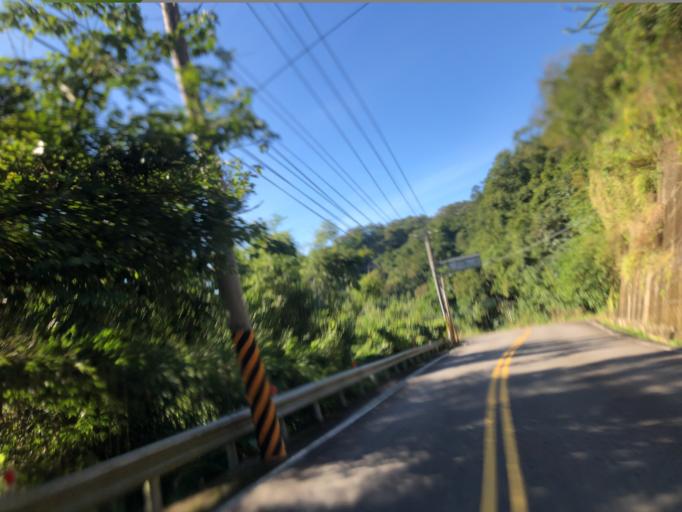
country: TW
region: Taiwan
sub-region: Miaoli
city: Miaoli
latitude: 24.5756
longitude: 120.9368
